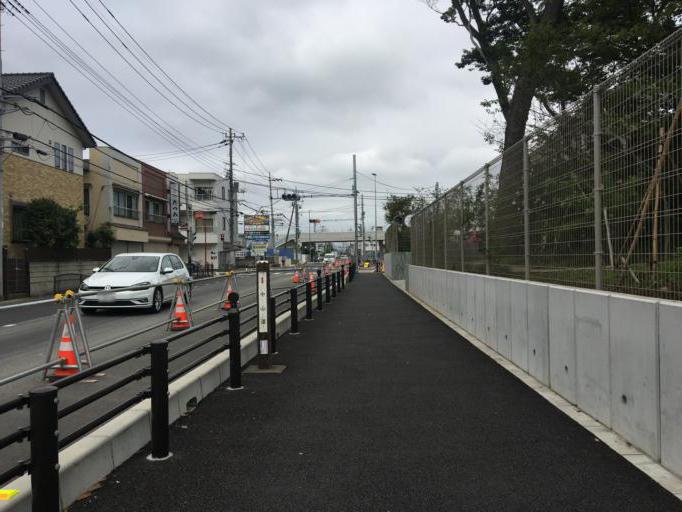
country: JP
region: Saitama
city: Ageoshimo
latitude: 35.9632
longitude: 139.5986
